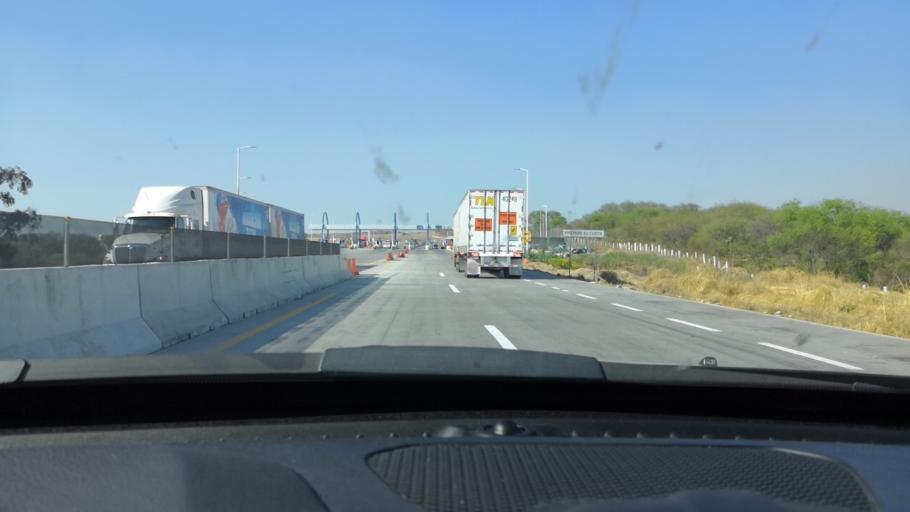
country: MX
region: Jalisco
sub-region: Zapotlanejo
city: La Mezquitera
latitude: 20.5705
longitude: -103.1015
